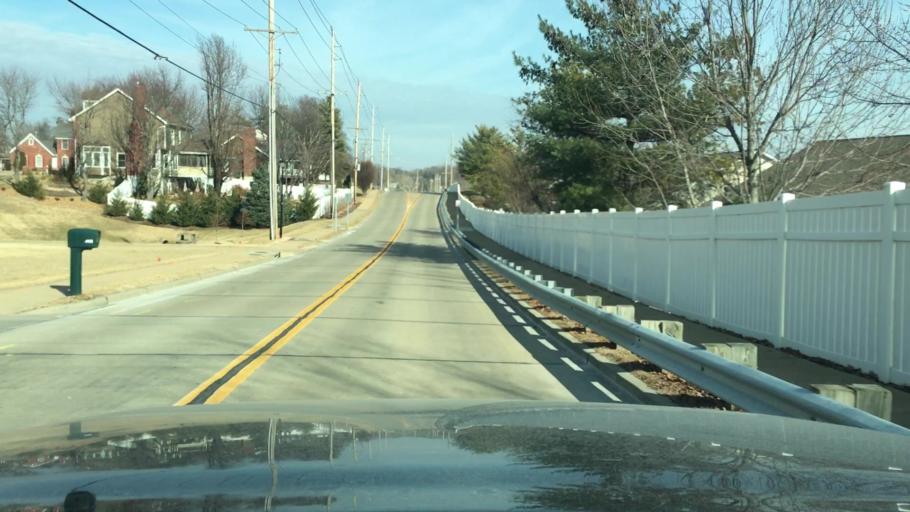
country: US
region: Missouri
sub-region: Saint Charles County
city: Saint Peters
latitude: 38.8025
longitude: -90.5600
